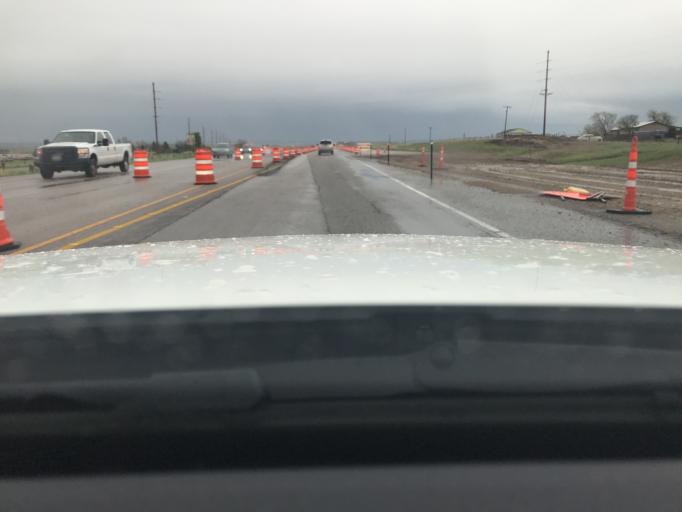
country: US
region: Wyoming
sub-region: Converse County
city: Douglas
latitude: 42.7807
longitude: -105.5066
